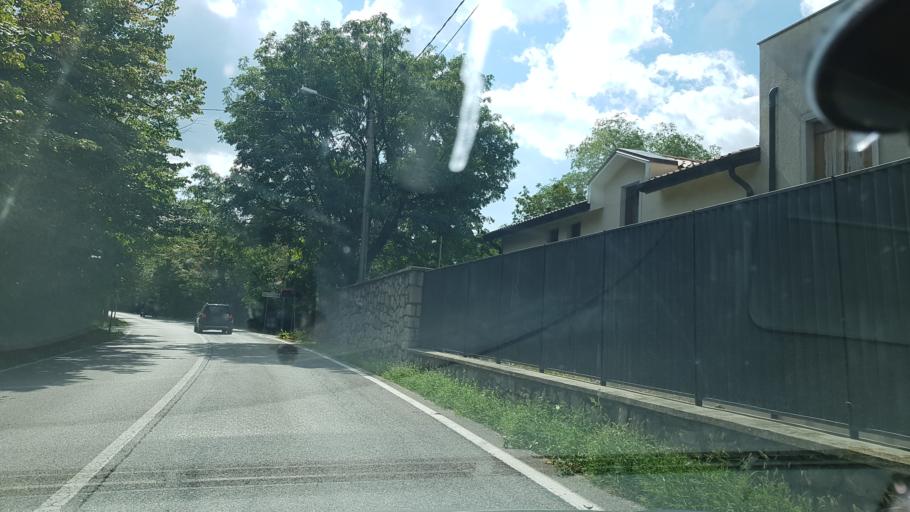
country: IT
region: Friuli Venezia Giulia
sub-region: Provincia di Trieste
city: Villa Opicina
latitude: 45.6939
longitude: 13.7956
